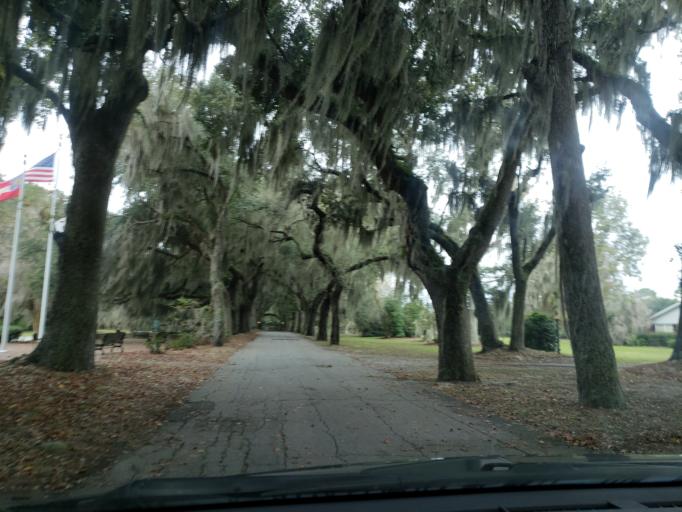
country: US
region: Georgia
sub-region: Chatham County
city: Montgomery
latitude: 31.9591
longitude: -81.0942
